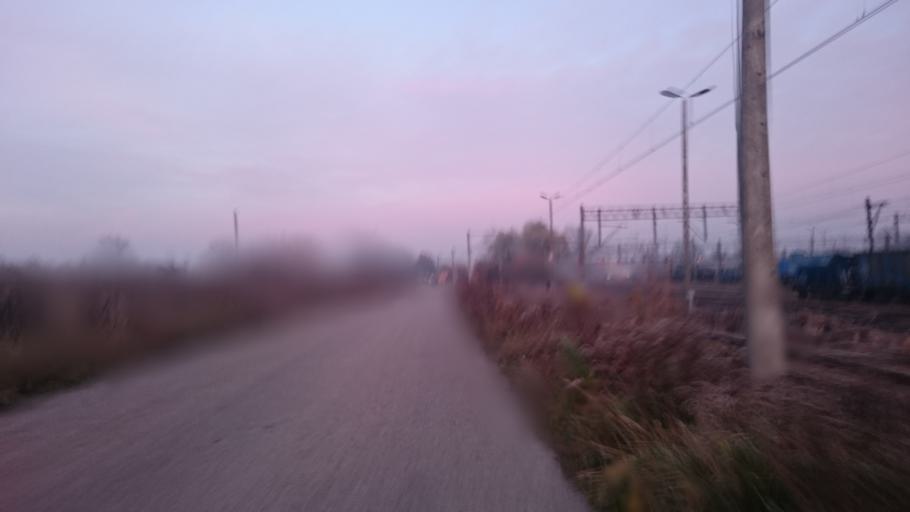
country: PL
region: Lesser Poland Voivodeship
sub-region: Powiat wielicki
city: Czarnochowice
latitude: 50.0274
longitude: 20.0059
